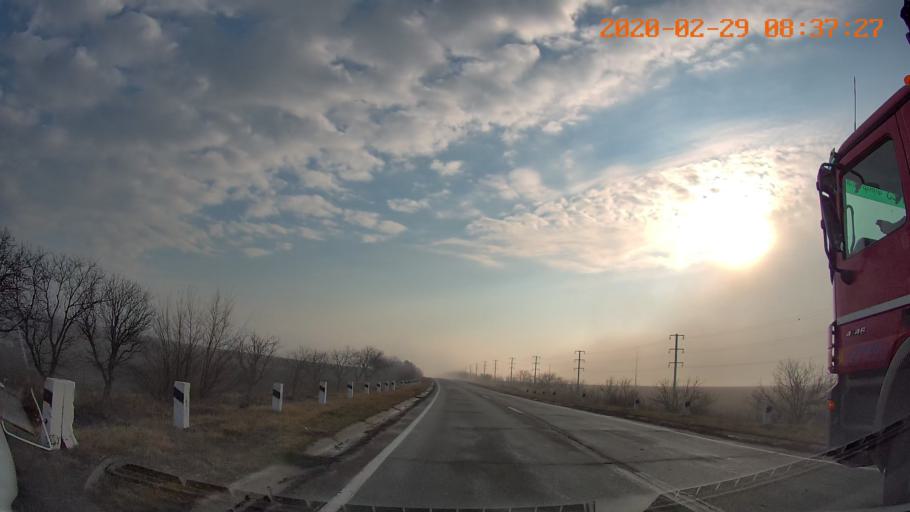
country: MD
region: Anenii Noi
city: Varnita
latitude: 46.9212
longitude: 29.3603
